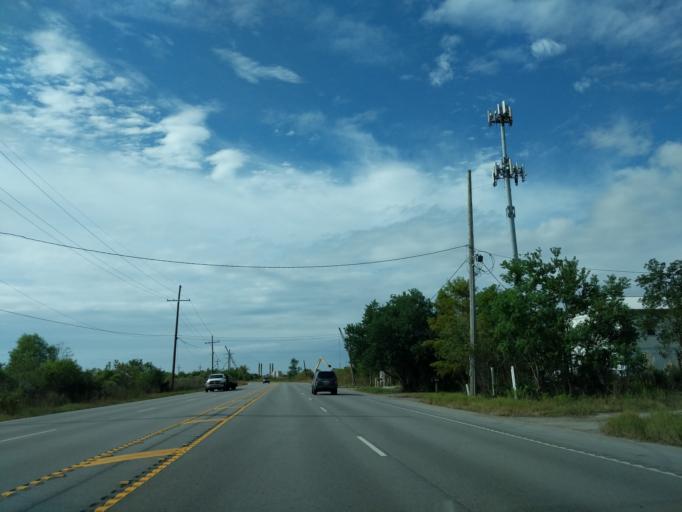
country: US
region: Louisiana
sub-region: Saint Tammany Parish
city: Eden Isle
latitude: 30.0743
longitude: -89.8414
